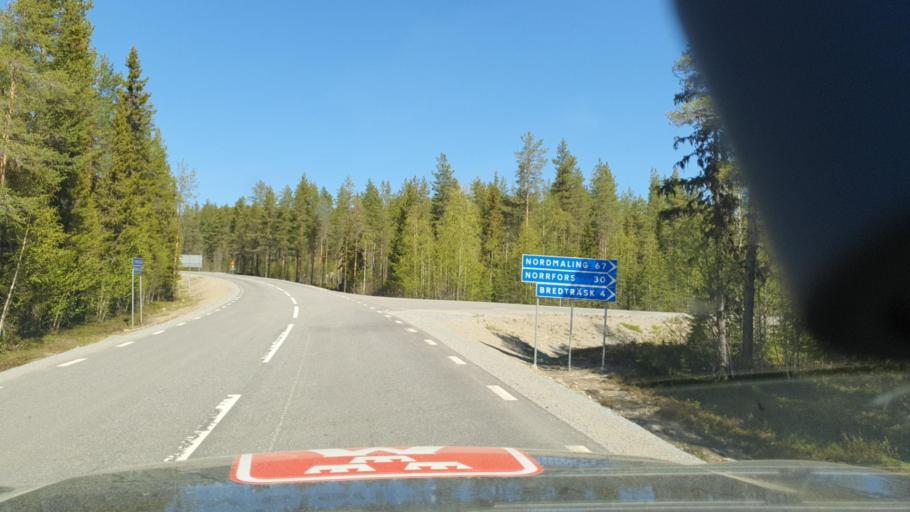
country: SE
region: Vaesternorrland
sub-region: OErnskoeldsviks Kommun
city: Bredbyn
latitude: 63.8847
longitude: 18.5193
